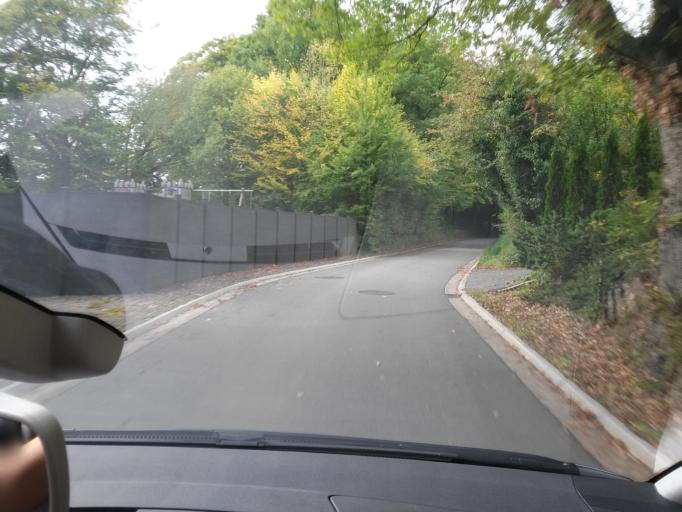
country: BE
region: Wallonia
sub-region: Province du Luxembourg
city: Arlon
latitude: 49.6531
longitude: 5.7752
